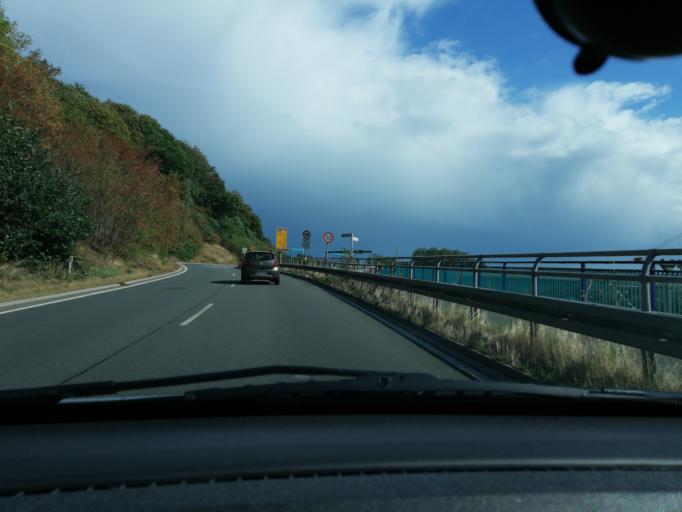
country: DE
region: North Rhine-Westphalia
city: Wetter (Ruhr)
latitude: 51.3919
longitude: 7.3776
